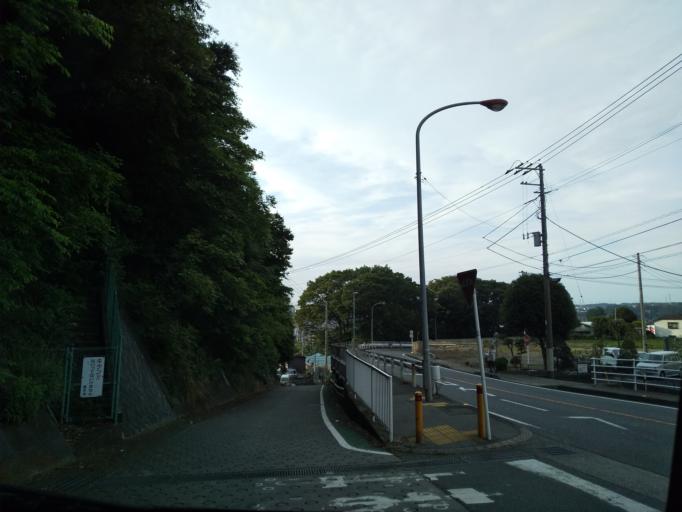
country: JP
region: Kanagawa
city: Zama
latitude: 35.5130
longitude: 139.3626
